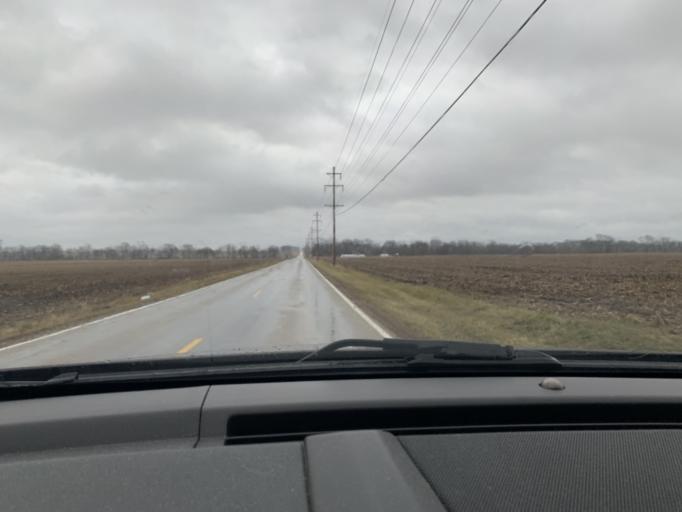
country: US
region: Ohio
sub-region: Ross County
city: Kingston
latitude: 39.4746
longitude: -82.8748
